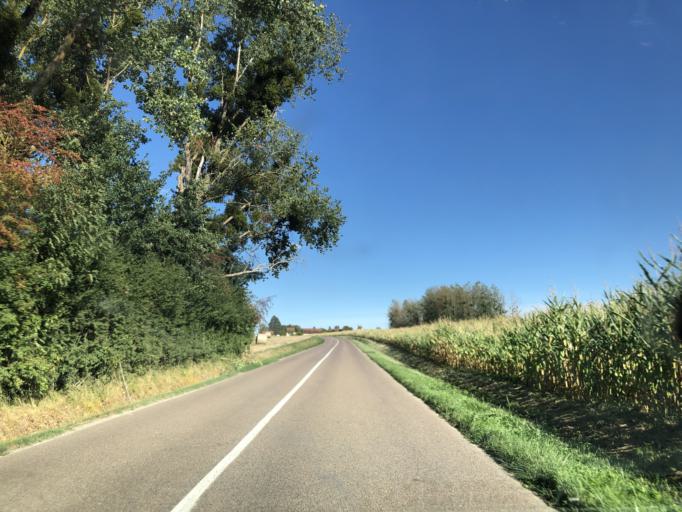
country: FR
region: Bourgogne
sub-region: Departement de l'Yonne
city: Seignelay
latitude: 47.9021
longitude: 3.6133
